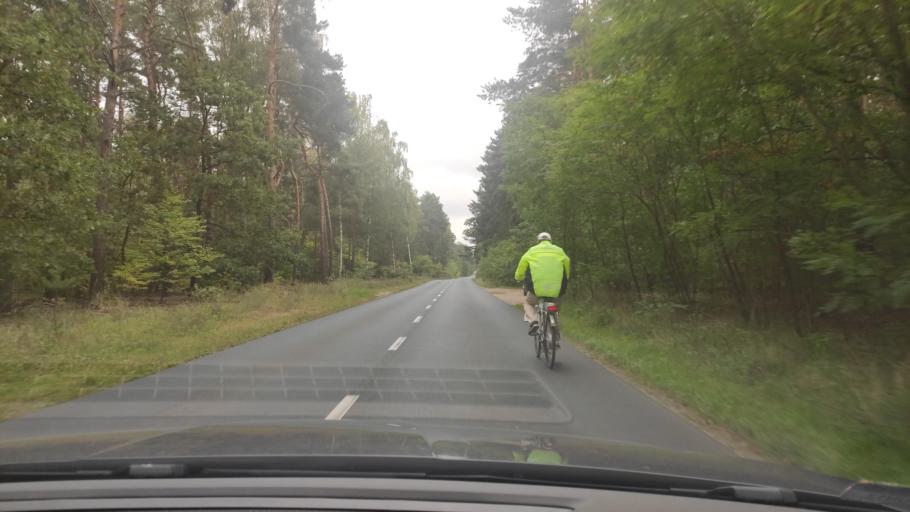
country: PL
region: Greater Poland Voivodeship
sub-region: Powiat poznanski
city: Swarzedz
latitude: 52.3898
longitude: 17.0357
